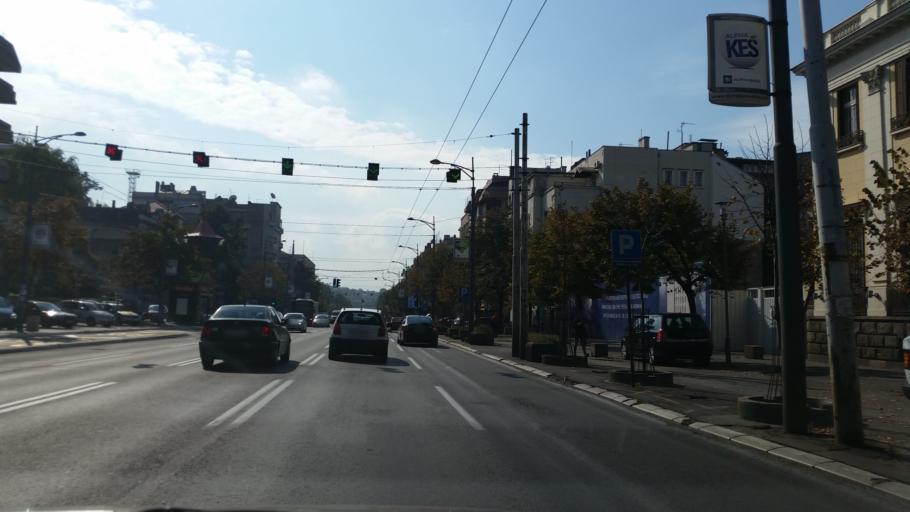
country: RS
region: Central Serbia
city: Belgrade
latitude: 44.8019
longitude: 20.4557
